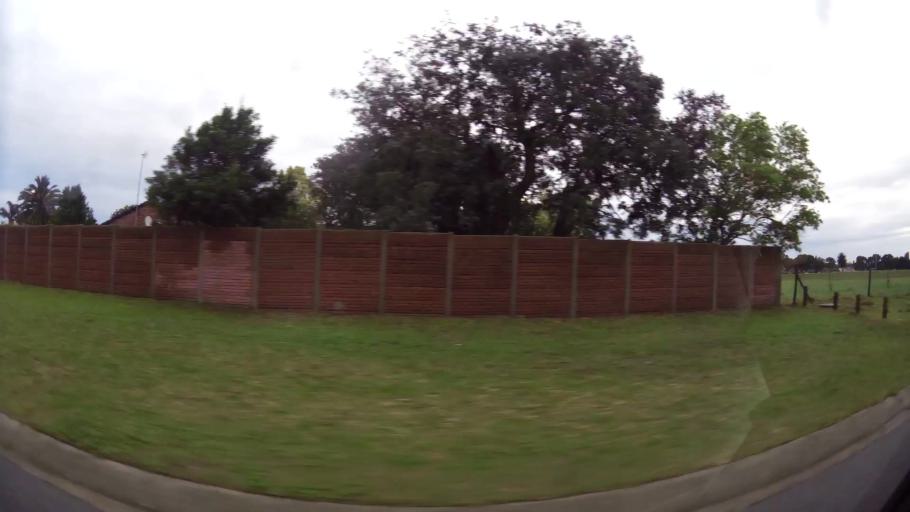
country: ZA
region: Eastern Cape
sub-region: Nelson Mandela Bay Metropolitan Municipality
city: Port Elizabeth
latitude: -33.9940
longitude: 25.5473
